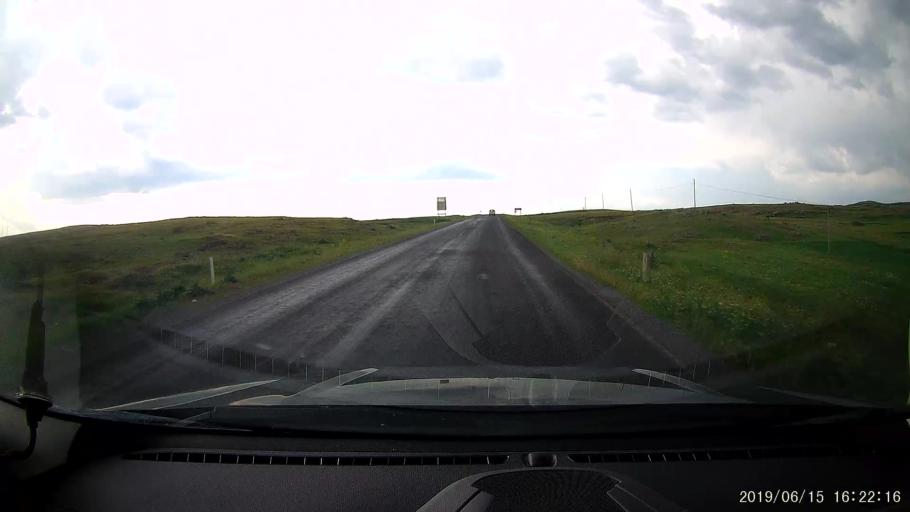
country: TR
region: Ardahan
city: Hanak
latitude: 41.1897
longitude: 42.8487
